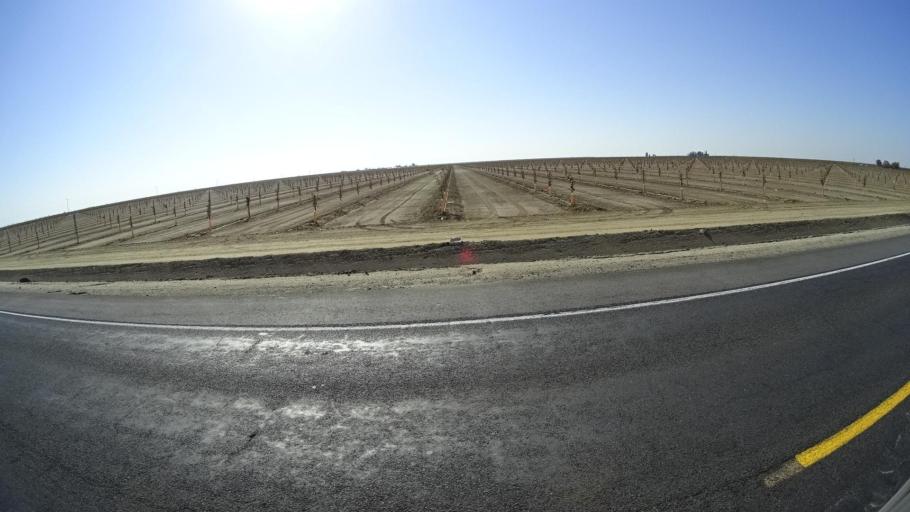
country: US
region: California
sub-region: Kern County
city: Delano
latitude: 35.7177
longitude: -119.3057
